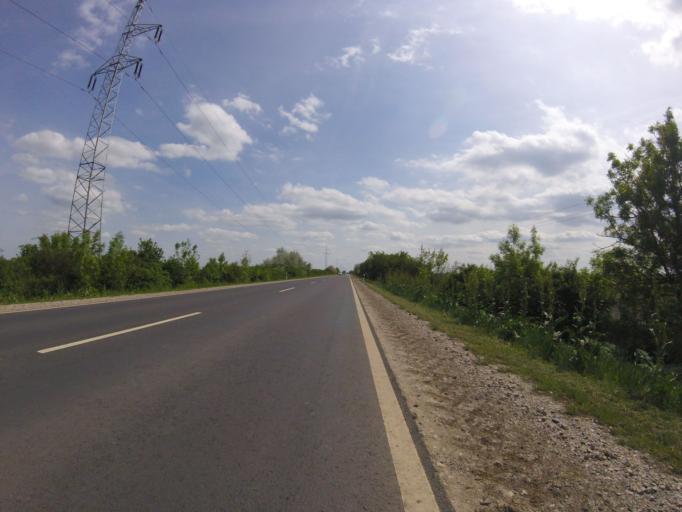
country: HU
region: Jasz-Nagykun-Szolnok
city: Zagyvarekas
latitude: 47.2506
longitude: 20.1066
